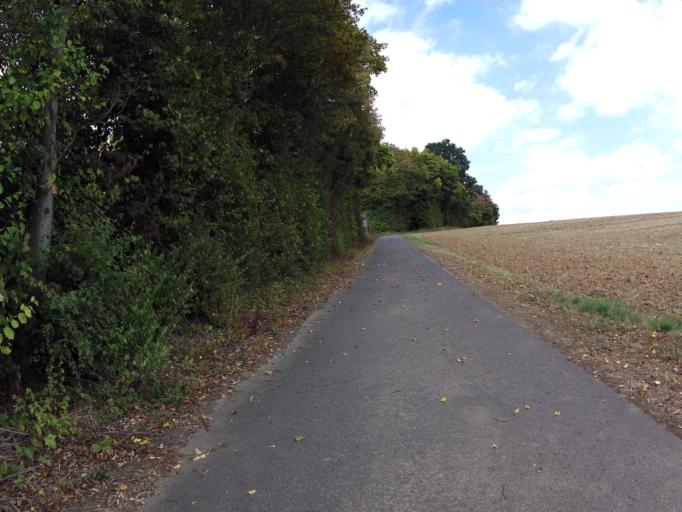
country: DE
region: Bavaria
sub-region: Regierungsbezirk Unterfranken
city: Hettstadt
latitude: 49.7894
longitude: 9.8175
